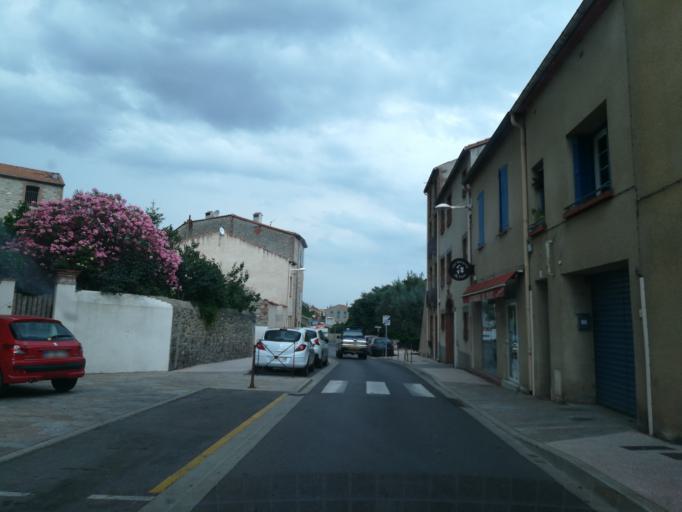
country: FR
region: Languedoc-Roussillon
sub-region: Departement des Pyrenees-Orientales
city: Ceret
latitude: 42.4945
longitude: 2.7434
